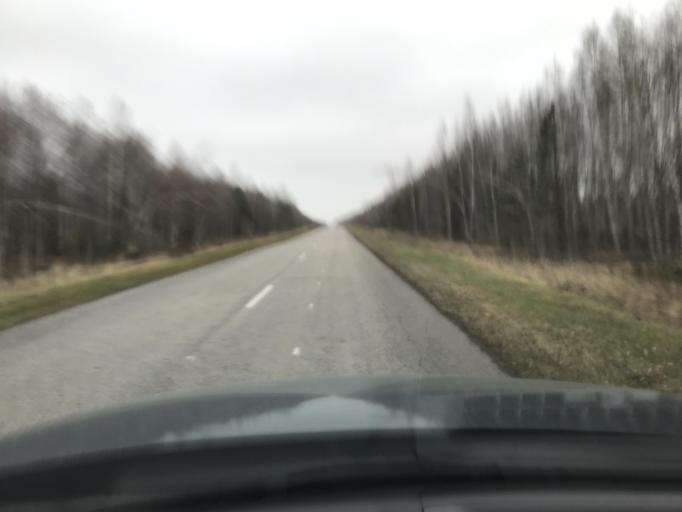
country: RU
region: Penza
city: Zemetchino
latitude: 53.6835
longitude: 42.6350
